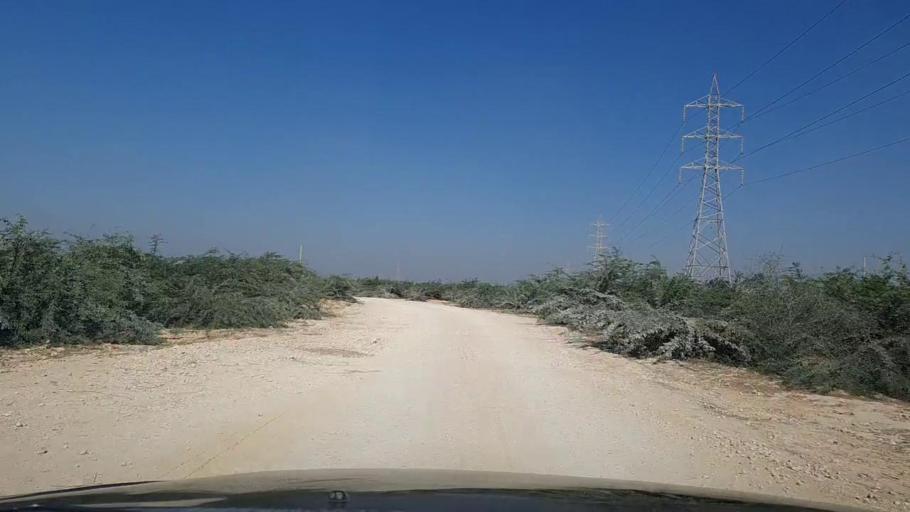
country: PK
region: Sindh
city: Thatta
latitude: 24.6286
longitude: 67.8341
